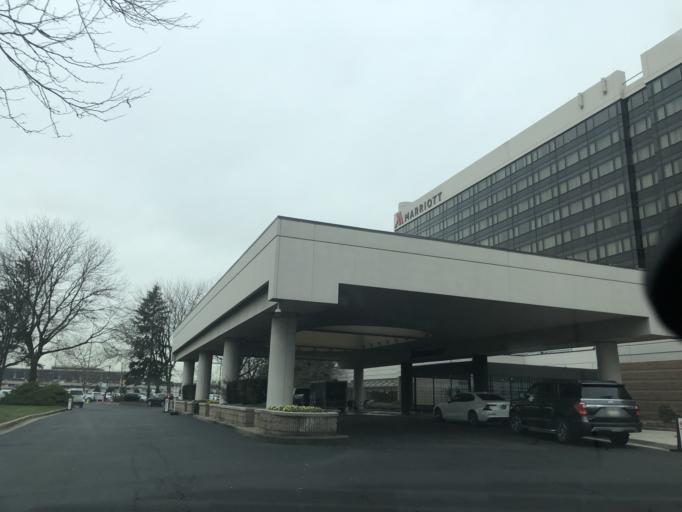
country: US
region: New Jersey
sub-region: Union County
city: Elizabeth
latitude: 40.6923
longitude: -74.1809
